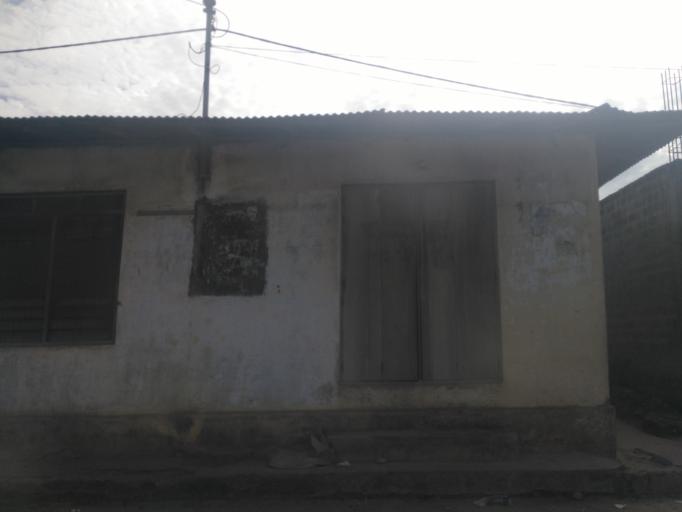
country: TZ
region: Zanzibar Urban/West
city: Zanzibar
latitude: -6.1562
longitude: 39.2089
